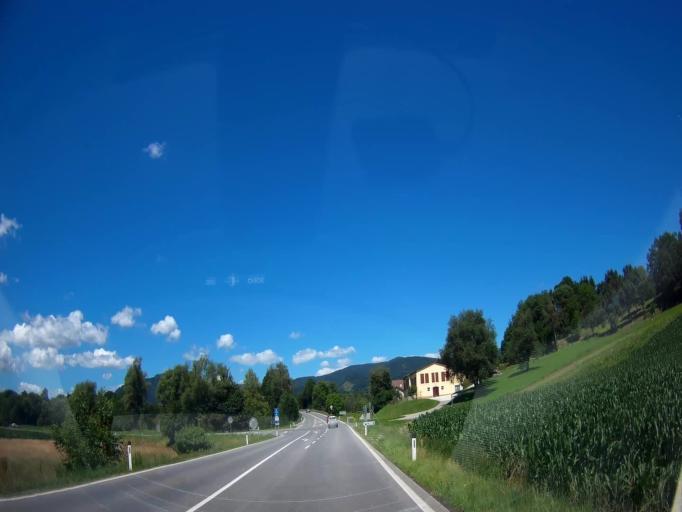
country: AT
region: Carinthia
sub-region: Politischer Bezirk Sankt Veit an der Glan
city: Sankt Veit an der Glan
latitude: 46.7646
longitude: 14.3834
